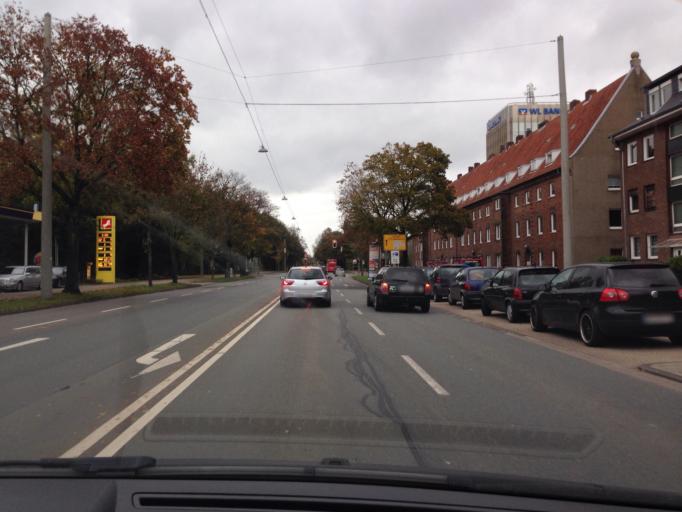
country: DE
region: North Rhine-Westphalia
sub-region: Regierungsbezirk Munster
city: Muenster
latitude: 51.9428
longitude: 7.6111
